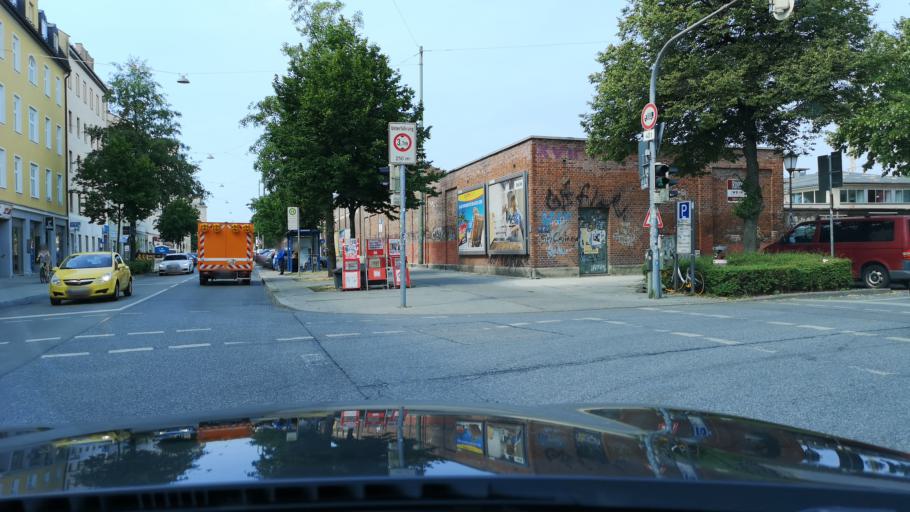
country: DE
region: Bavaria
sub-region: Upper Bavaria
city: Munich
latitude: 48.1226
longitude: 11.5593
